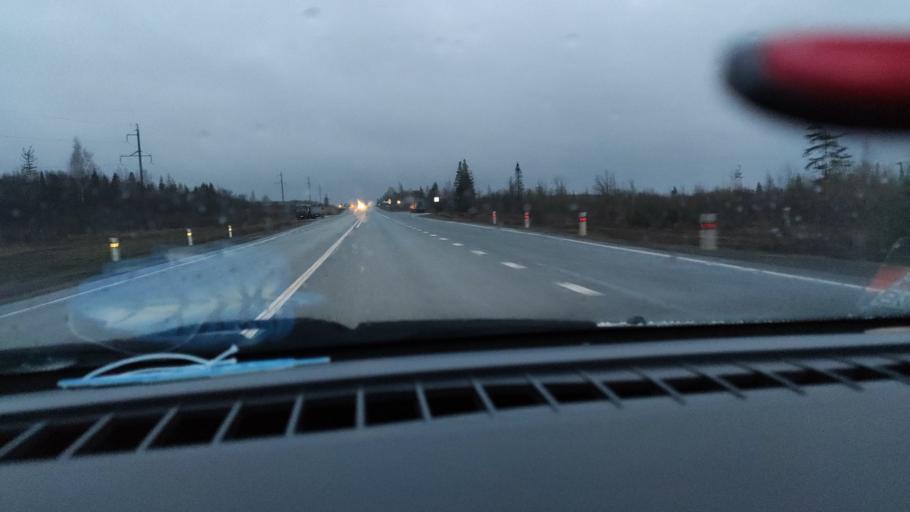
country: RU
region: Udmurtiya
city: Alnashi
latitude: 56.2612
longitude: 52.3722
